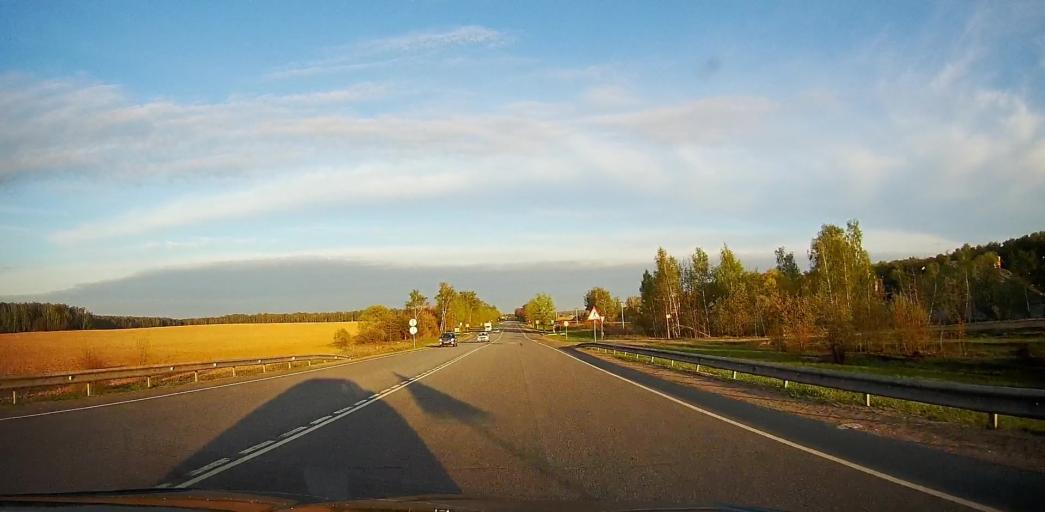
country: RU
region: Moskovskaya
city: Troitskoye
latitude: 55.2164
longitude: 38.5905
